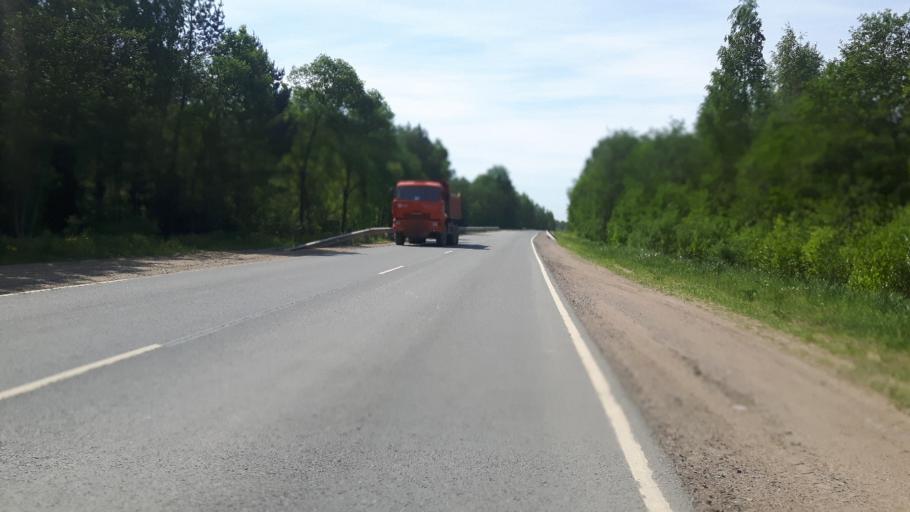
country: RU
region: Leningrad
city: Vistino
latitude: 59.6813
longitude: 28.4568
